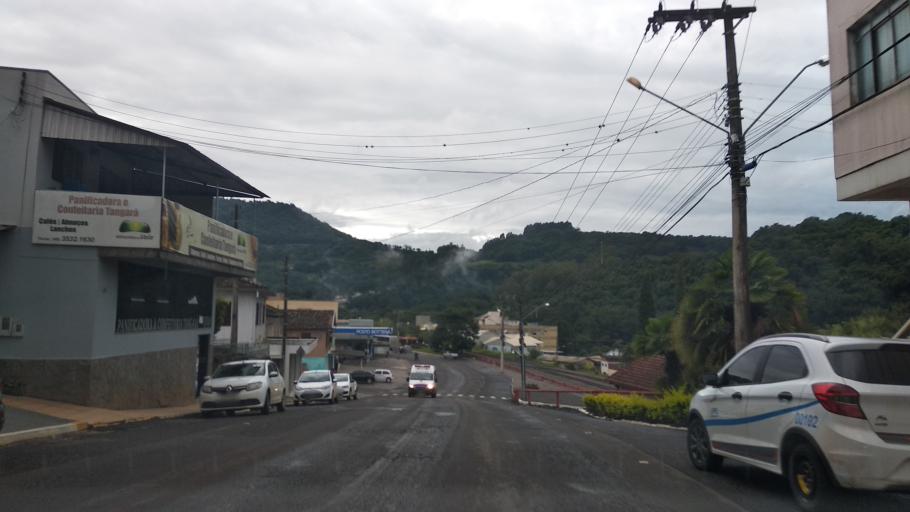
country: BR
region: Santa Catarina
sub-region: Videira
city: Videira
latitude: -27.1034
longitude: -51.2459
